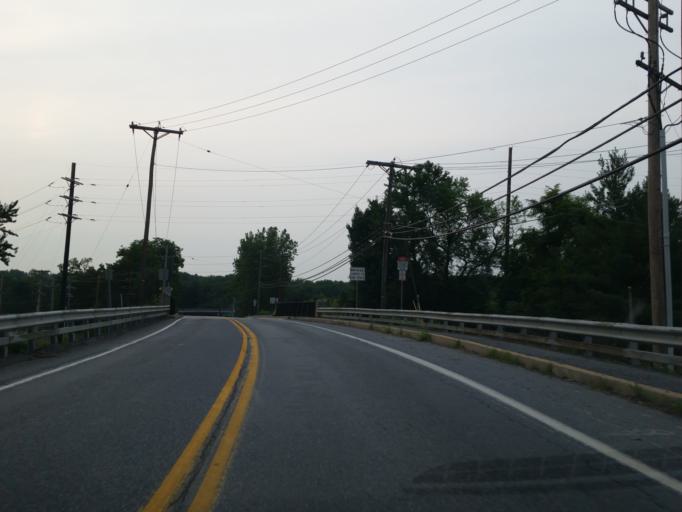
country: US
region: Pennsylvania
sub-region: Lebanon County
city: Annville
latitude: 40.3326
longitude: -76.5167
